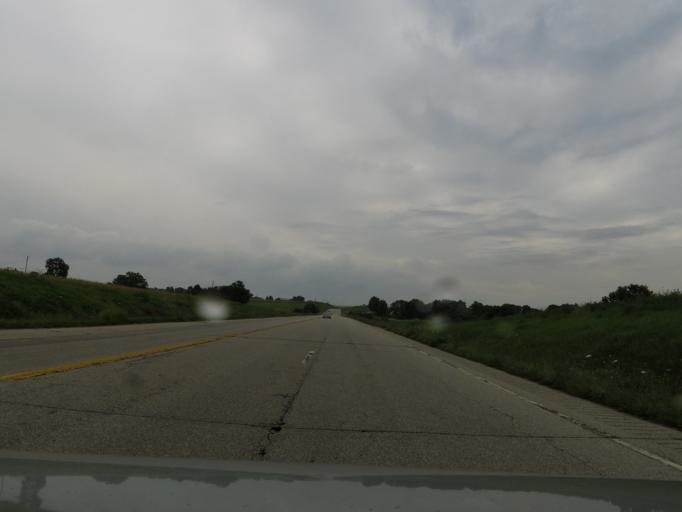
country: US
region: Kentucky
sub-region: Mason County
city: Maysville
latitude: 38.5530
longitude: -83.8229
